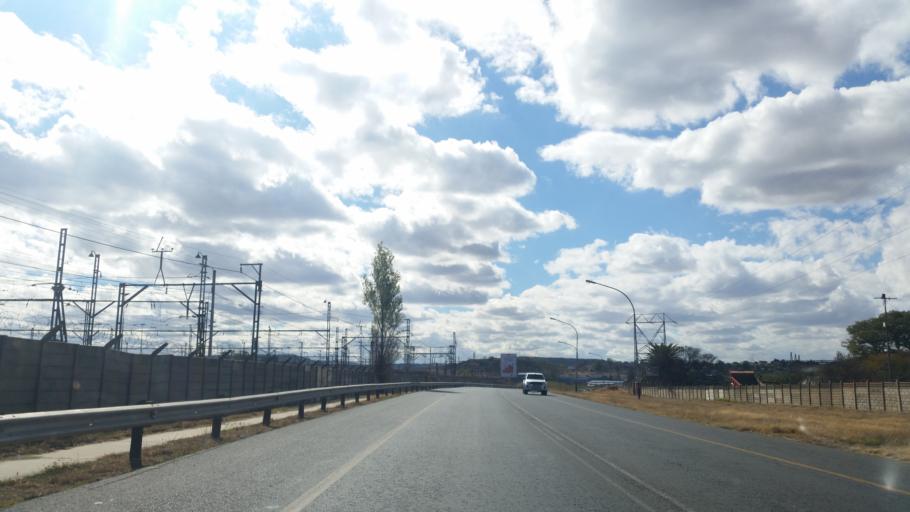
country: ZA
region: KwaZulu-Natal
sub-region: uThukela District Municipality
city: Ladysmith
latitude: -28.5419
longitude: 29.7951
